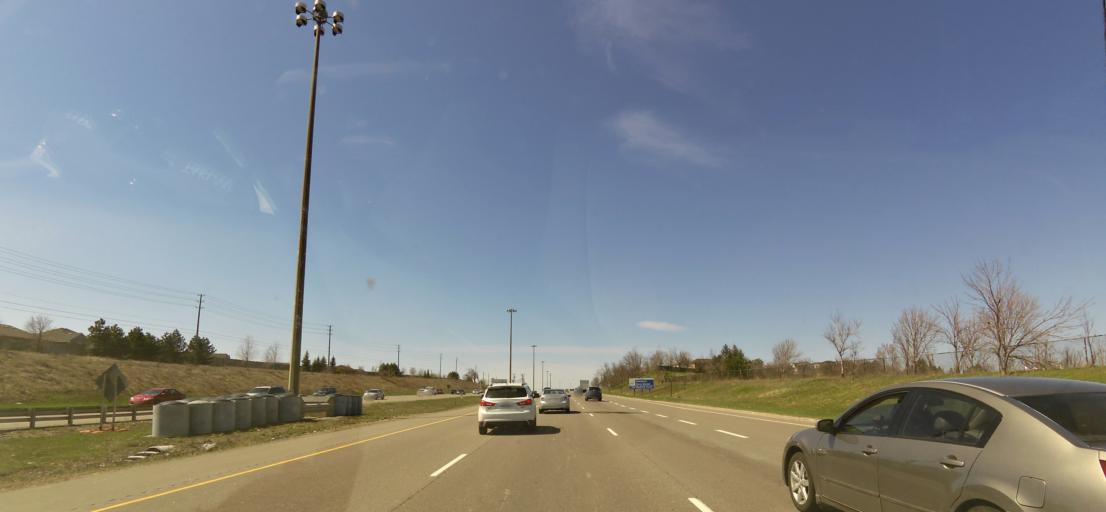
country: CA
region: Ontario
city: Brampton
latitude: 43.7189
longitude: -79.7561
